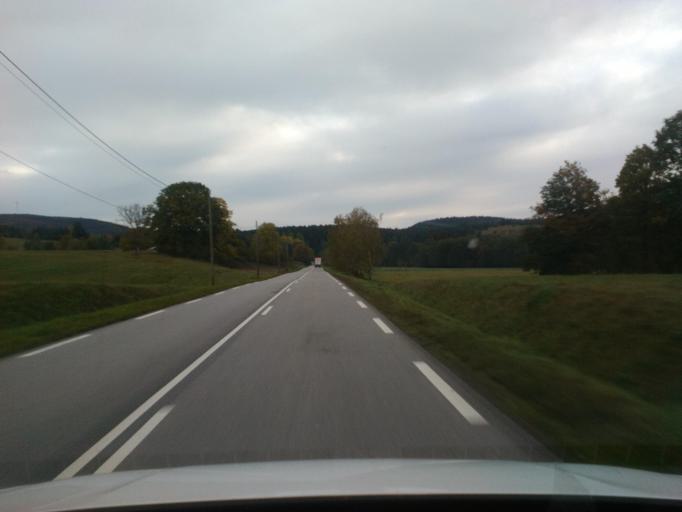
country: FR
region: Lorraine
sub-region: Departement des Vosges
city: Ban-de-Laveline
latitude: 48.3136
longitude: 7.0904
